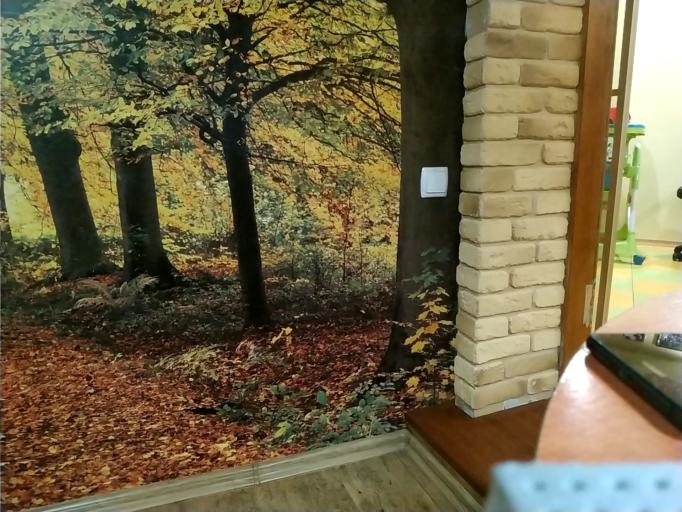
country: RU
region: Tverskaya
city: Zubtsov
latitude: 56.2537
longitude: 34.6996
